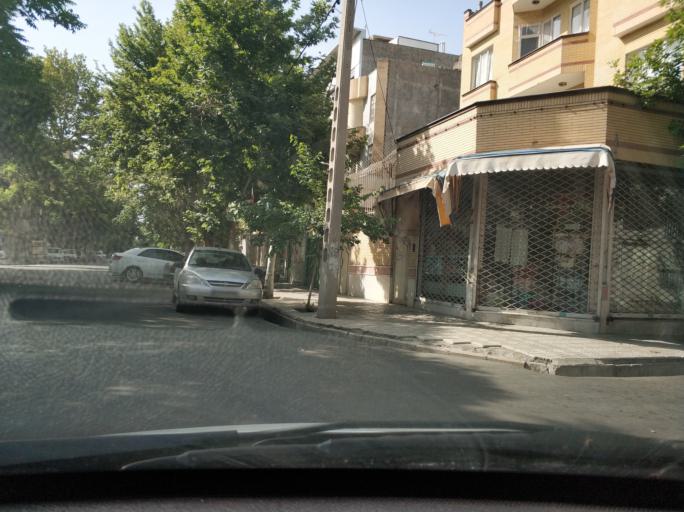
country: IR
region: Razavi Khorasan
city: Mashhad
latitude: 36.2720
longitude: 59.5979
